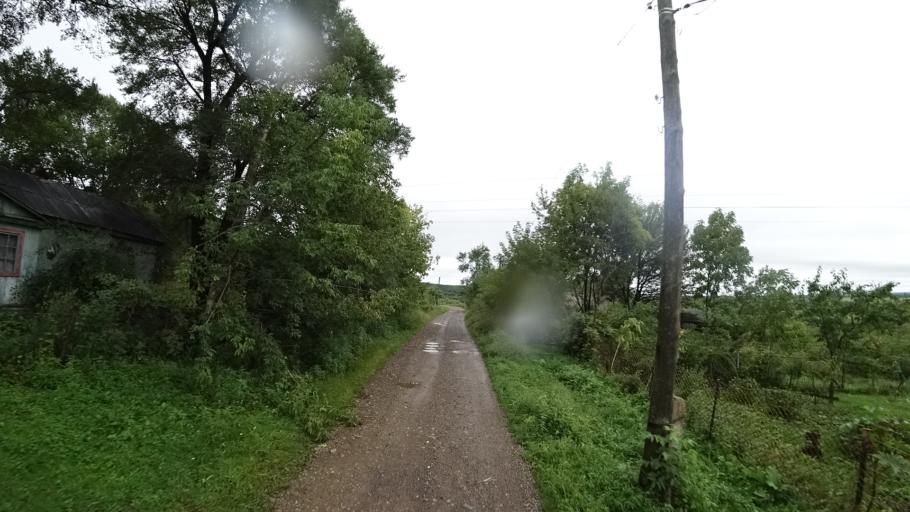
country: RU
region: Primorskiy
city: Monastyrishche
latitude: 44.2627
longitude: 132.4050
